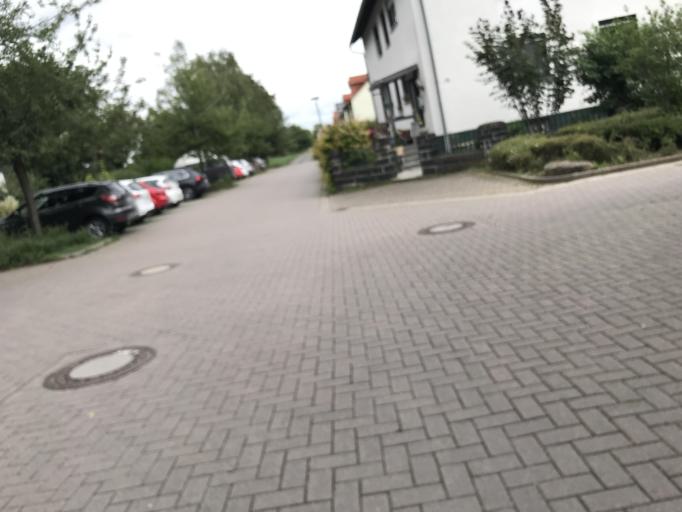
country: DE
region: Hesse
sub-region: Regierungsbezirk Darmstadt
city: Friedberg
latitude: 50.3337
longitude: 8.7653
